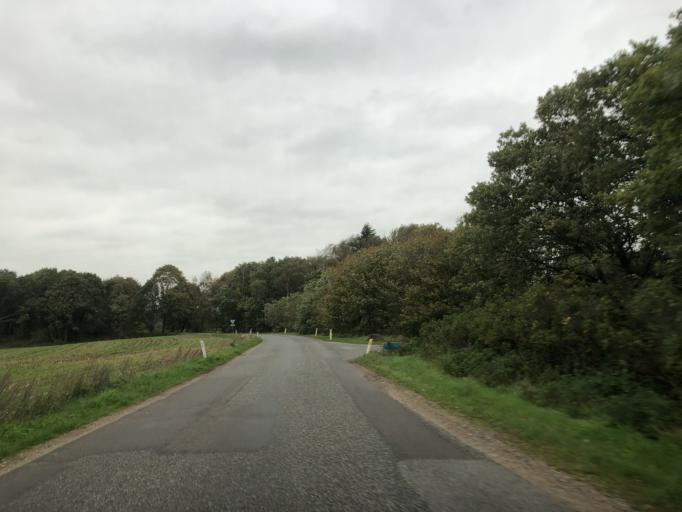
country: DK
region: Central Jutland
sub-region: Viborg Kommune
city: Viborg
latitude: 56.3870
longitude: 9.3050
